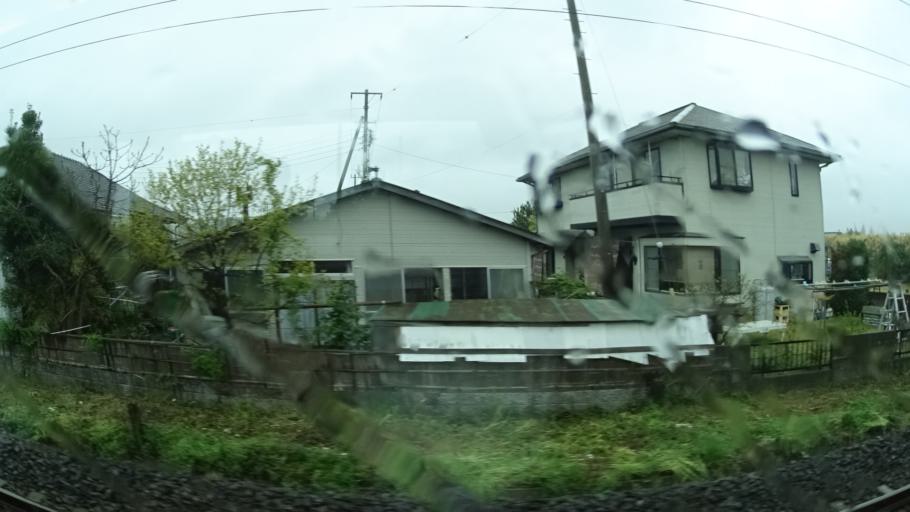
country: JP
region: Ibaraki
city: Kitaibaraki
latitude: 36.8217
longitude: 140.7695
